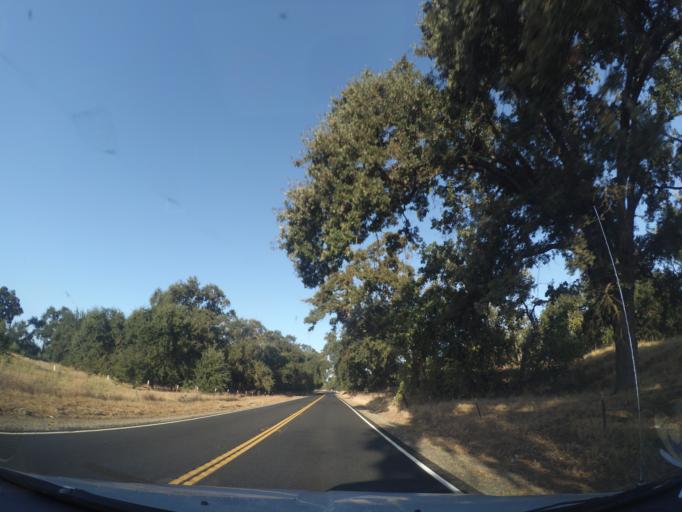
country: US
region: California
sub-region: Merced County
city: Winton
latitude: 37.5139
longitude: -120.4618
